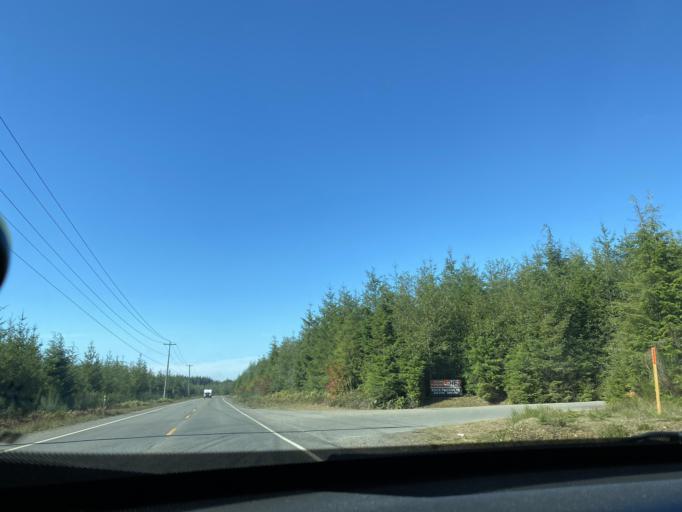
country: US
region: Washington
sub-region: Clallam County
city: Forks
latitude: 47.9637
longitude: -124.4204
